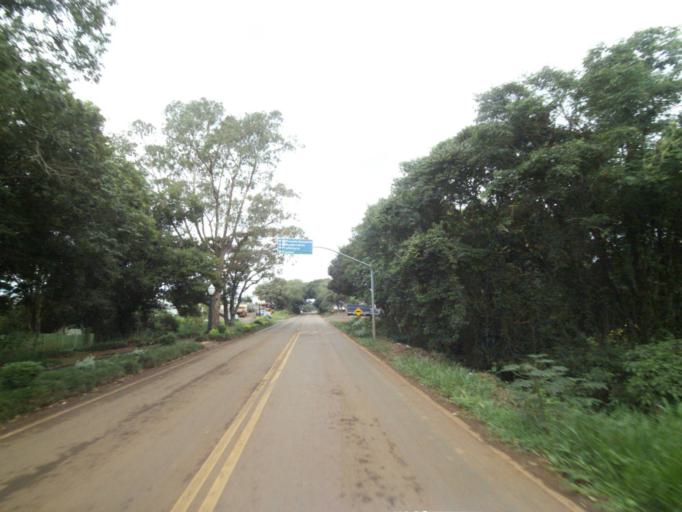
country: BR
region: Parana
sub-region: Guaraniacu
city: Guaraniacu
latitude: -25.0965
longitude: -52.8791
